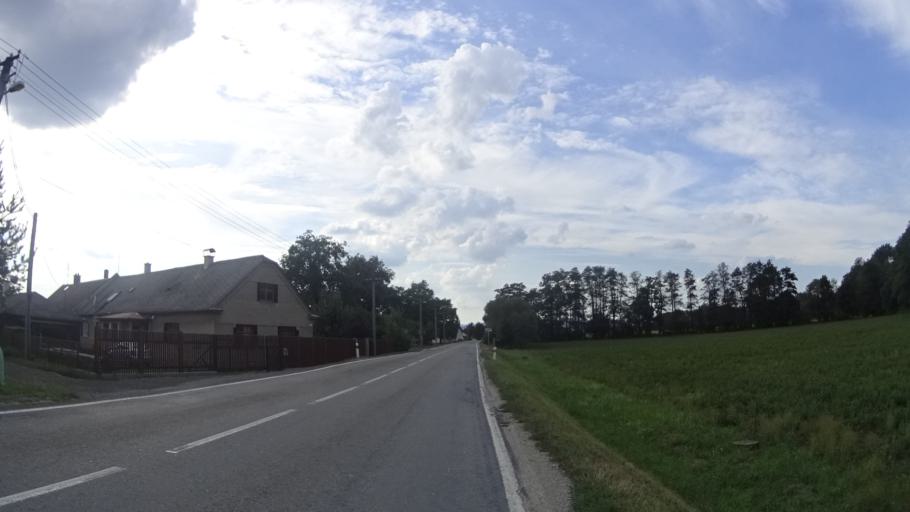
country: CZ
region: Olomoucky
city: Lestina
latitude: 49.8613
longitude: 16.9423
